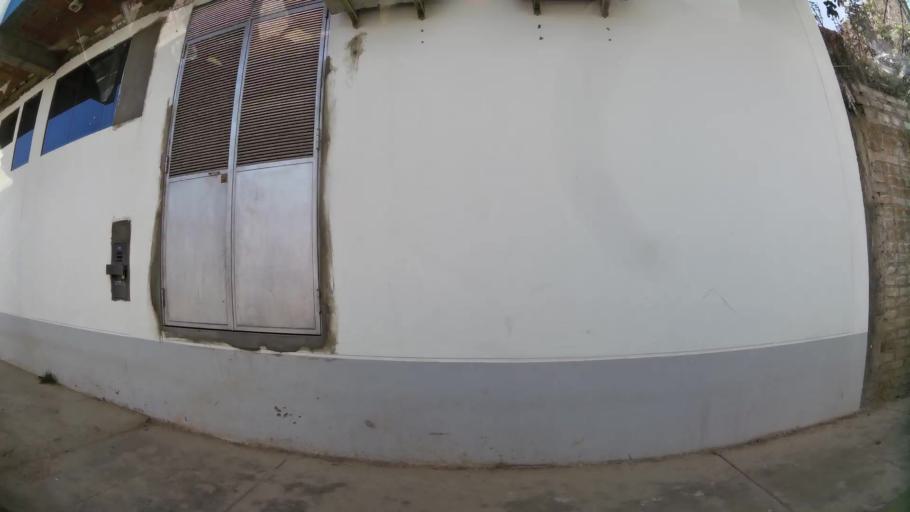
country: PE
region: Junin
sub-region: Provincia de Huancayo
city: El Tambo
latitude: -12.0671
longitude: -75.2221
